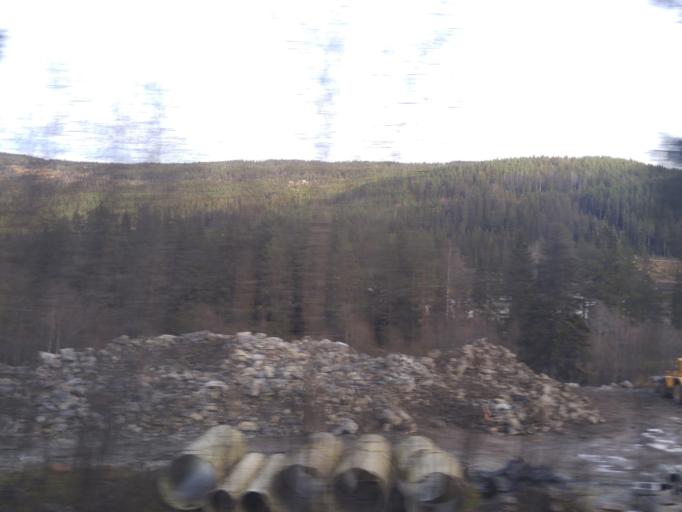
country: NO
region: Oppland
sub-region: Nord-Aurdal
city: Fagernes
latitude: 61.0005
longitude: 9.2096
